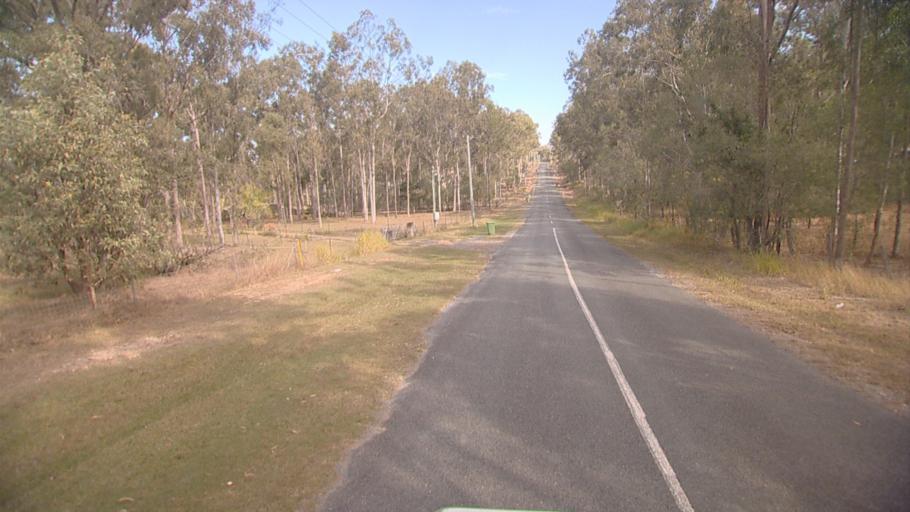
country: AU
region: Queensland
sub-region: Logan
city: North Maclean
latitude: -27.7391
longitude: 152.9785
